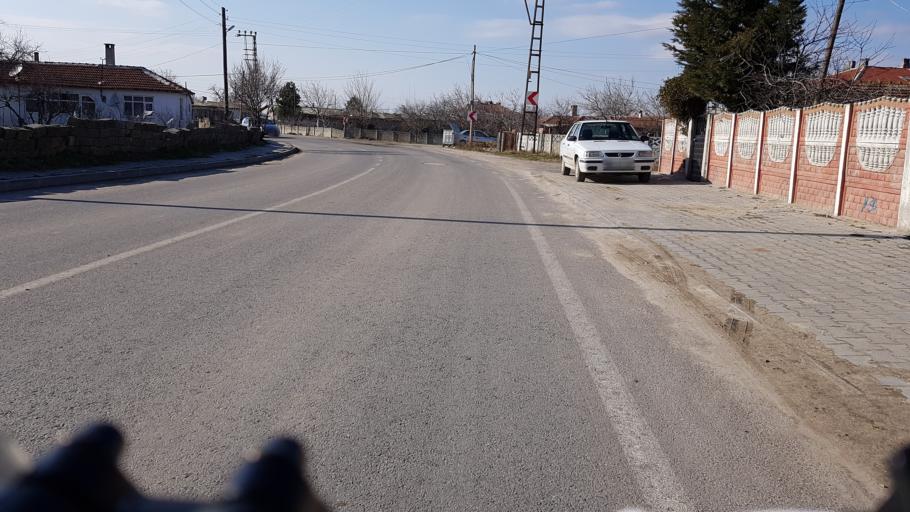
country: TR
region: Tekirdag
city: Saray
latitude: 41.3698
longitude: 27.8633
